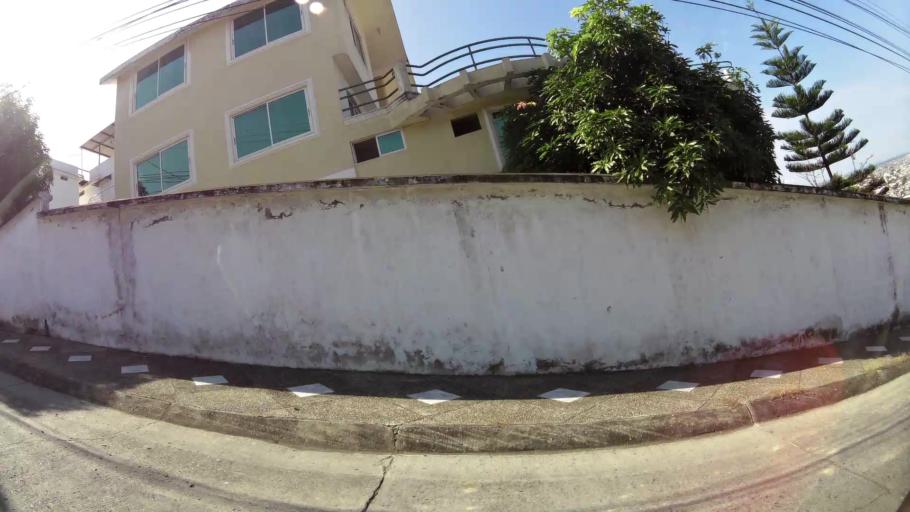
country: EC
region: Guayas
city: Guayaquil
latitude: -2.1835
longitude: -79.9161
